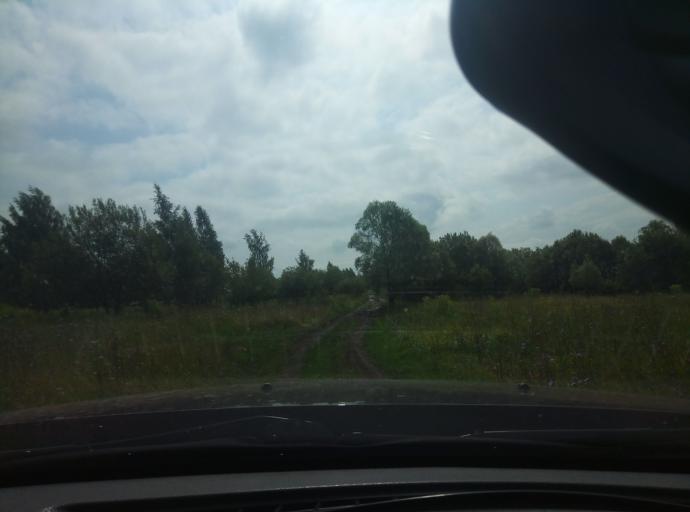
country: RU
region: Tula
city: Shvartsevskiy
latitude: 54.0793
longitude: 38.0222
